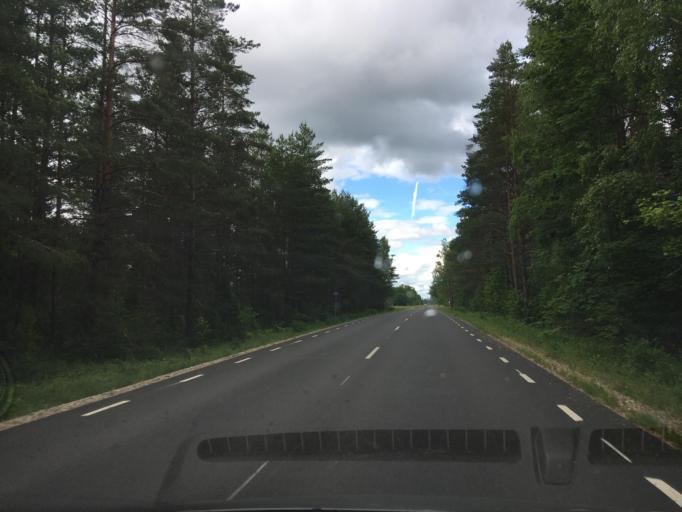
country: EE
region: Paernumaa
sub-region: Audru vald
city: Audru
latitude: 58.6044
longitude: 24.1921
